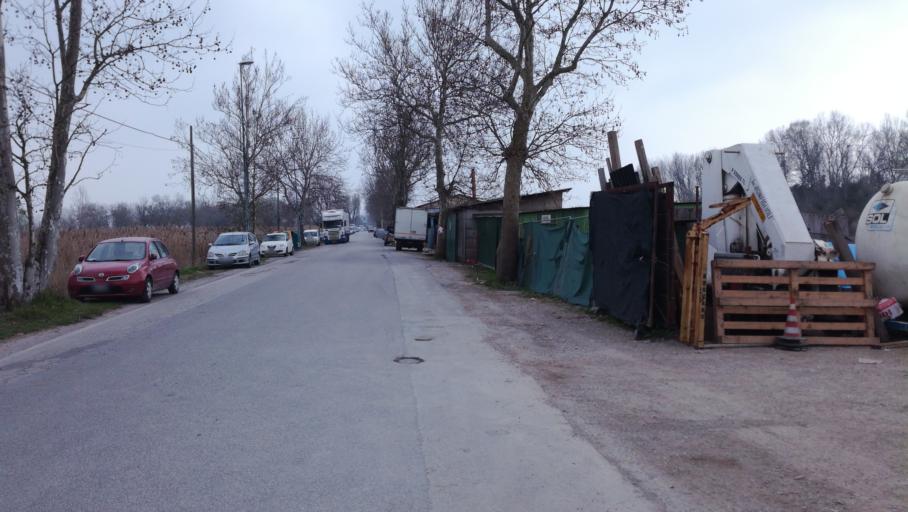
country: IT
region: Veneto
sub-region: Provincia di Venezia
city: Campalto
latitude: 45.4693
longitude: 12.2743
